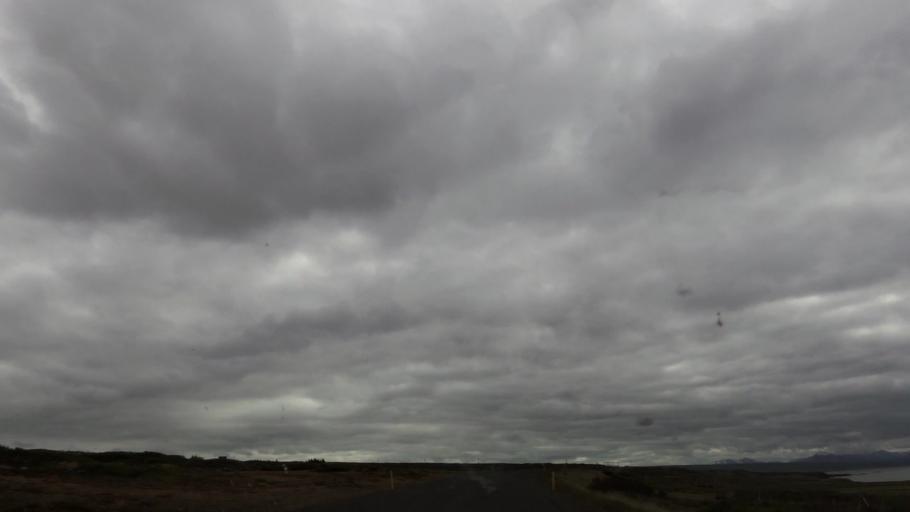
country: IS
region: West
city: Borgarnes
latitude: 65.2059
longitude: -21.7171
